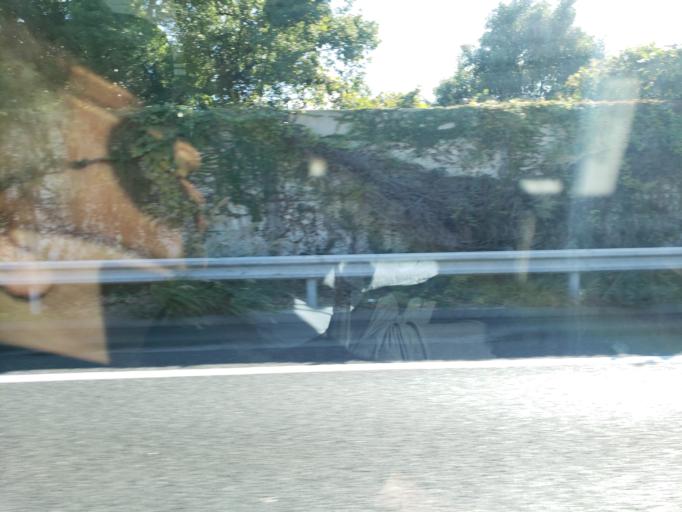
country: JP
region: Hyogo
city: Sumoto
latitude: 34.3540
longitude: 134.8531
